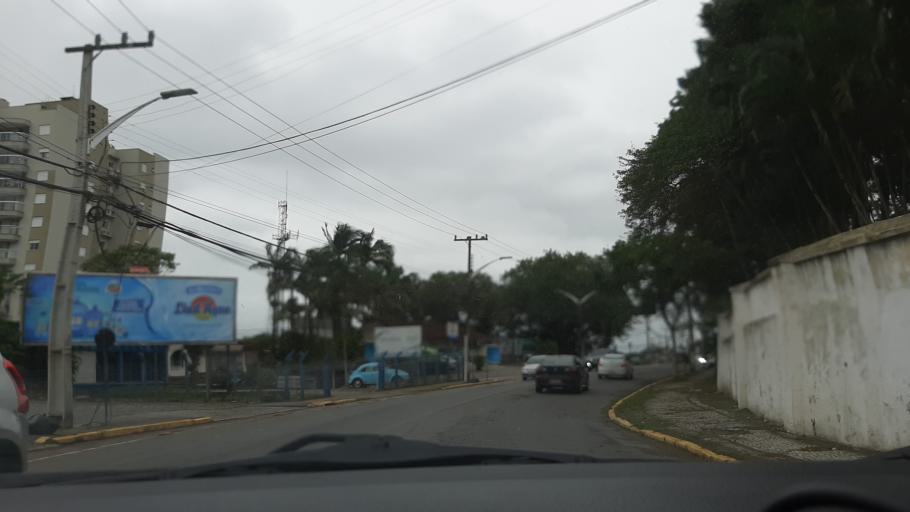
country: BR
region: Santa Catarina
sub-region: Joinville
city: Joinville
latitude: -26.3117
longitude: -48.8564
